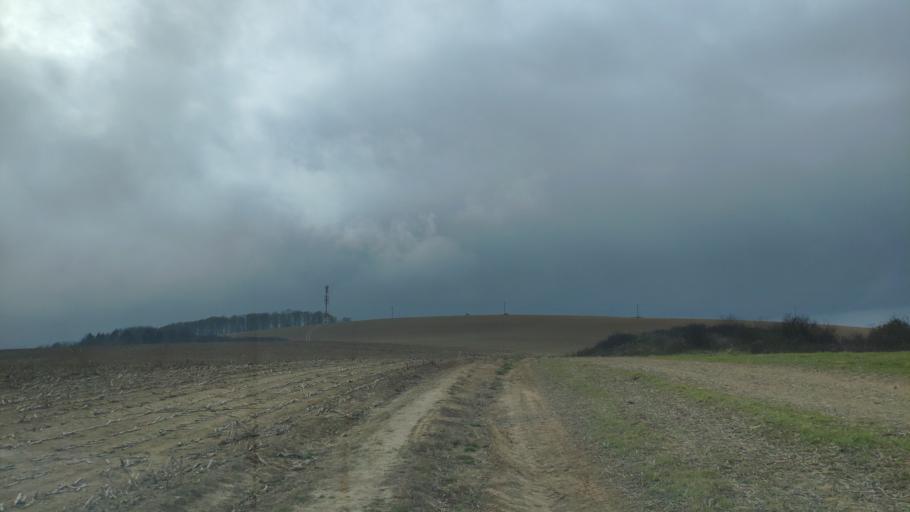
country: SK
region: Presovsky
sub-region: Okres Presov
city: Presov
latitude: 49.0096
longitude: 21.2040
